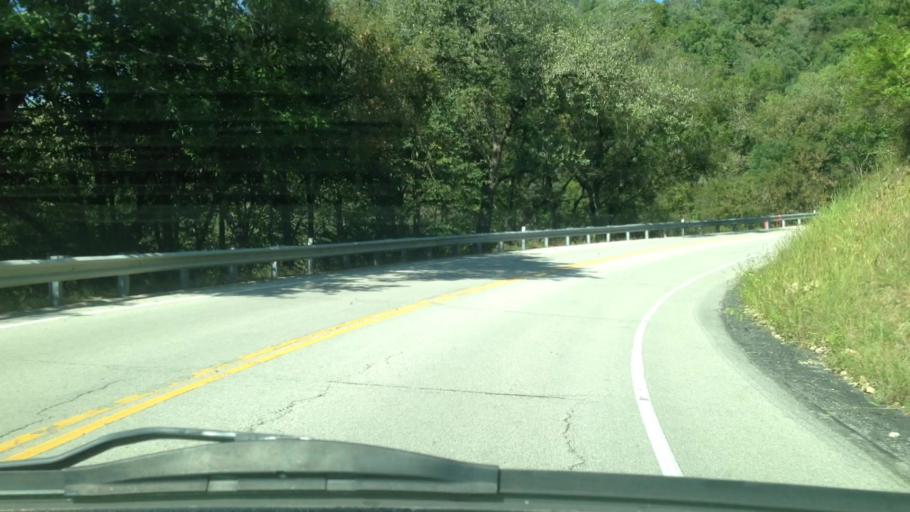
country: US
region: Minnesota
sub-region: Fillmore County
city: Rushford
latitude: 43.6856
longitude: -91.7864
